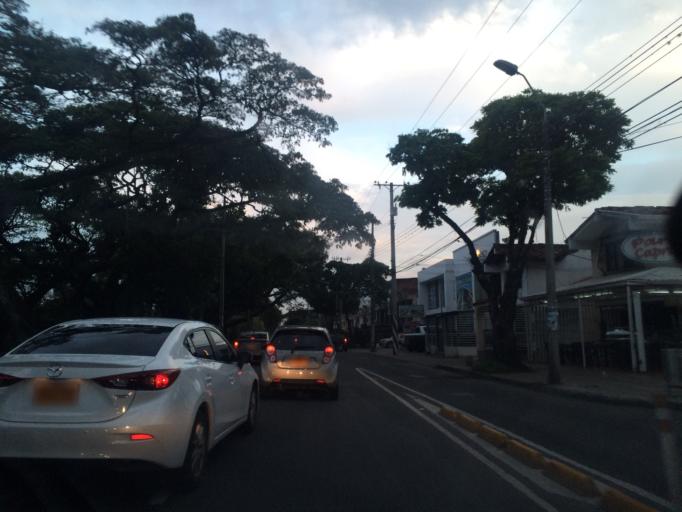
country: CO
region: Valle del Cauca
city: Cali
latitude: 3.3937
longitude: -76.5420
